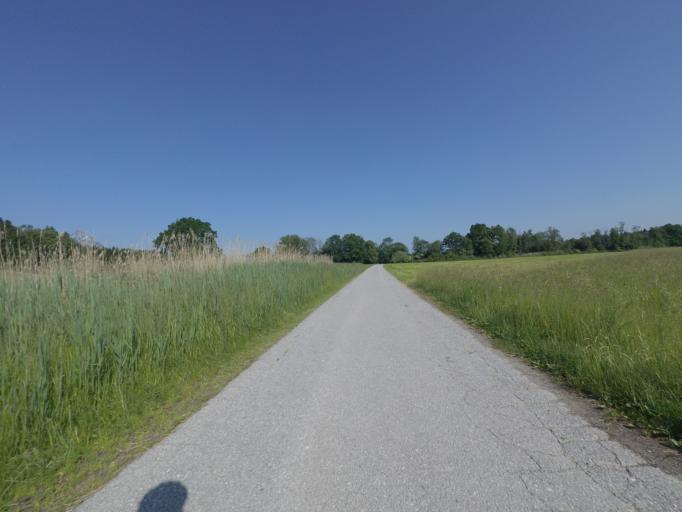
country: DE
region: Bavaria
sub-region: Upper Bavaria
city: Piding
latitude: 47.7627
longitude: 12.9762
